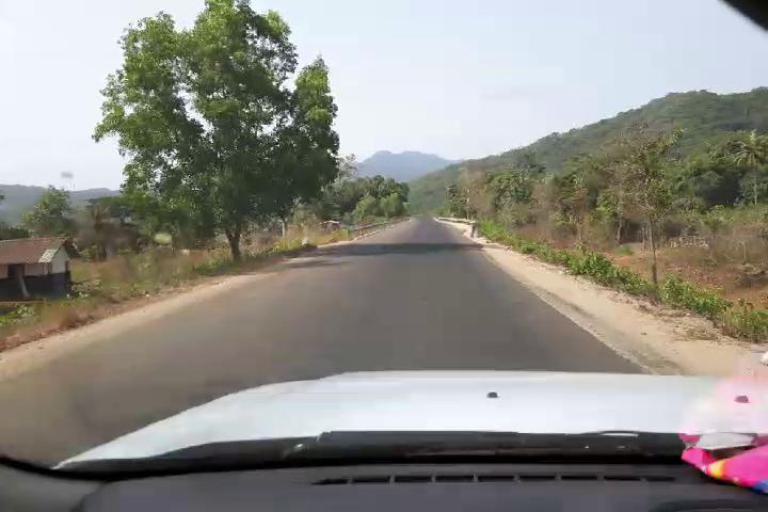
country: SL
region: Western Area
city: Hastings
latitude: 8.2735
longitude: -13.1577
